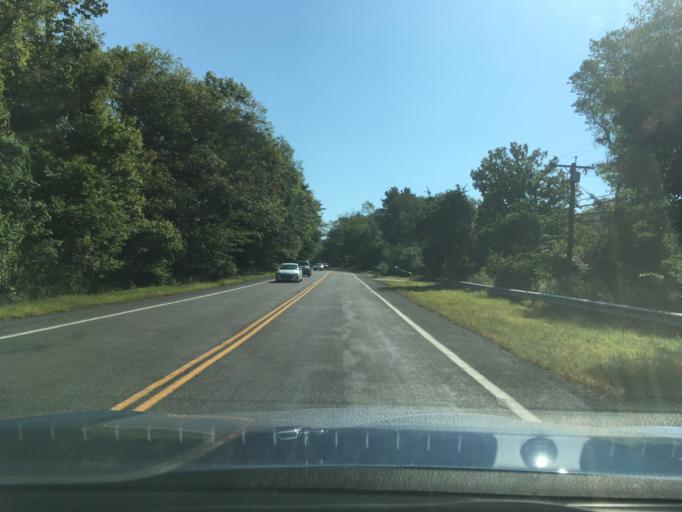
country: US
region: Rhode Island
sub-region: Washington County
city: Exeter
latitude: 41.5801
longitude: -71.5670
